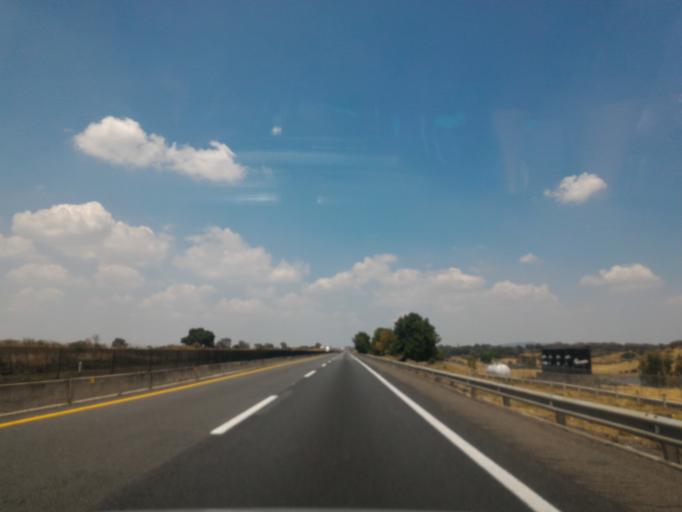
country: MX
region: Jalisco
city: Tepatitlan de Morelos
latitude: 20.8772
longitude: -102.7390
